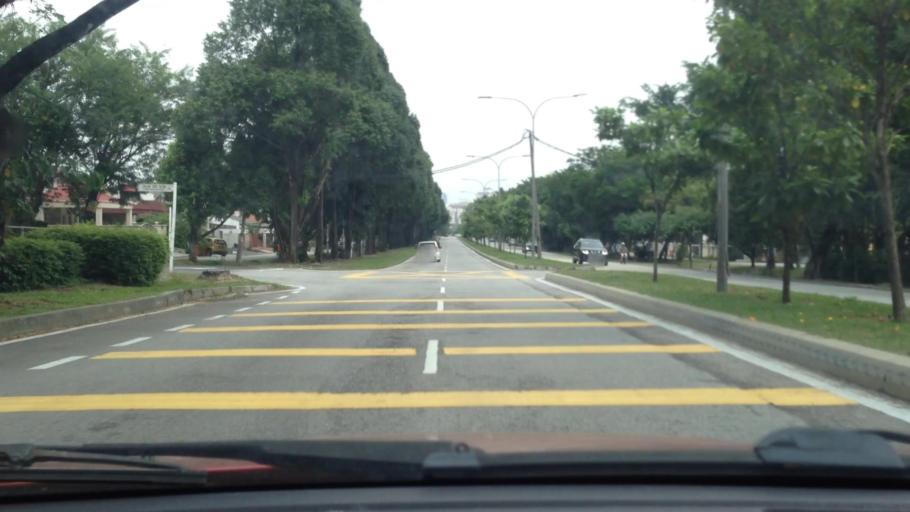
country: MY
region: Selangor
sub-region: Petaling
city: Petaling Jaya
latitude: 3.0997
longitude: 101.6072
